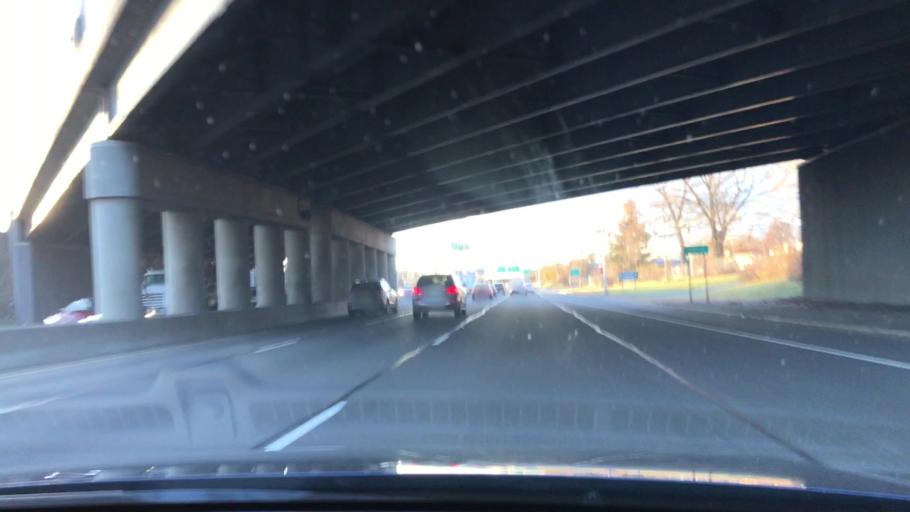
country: US
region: New Jersey
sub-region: Bergen County
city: Maywood
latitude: 40.8906
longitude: -74.0705
